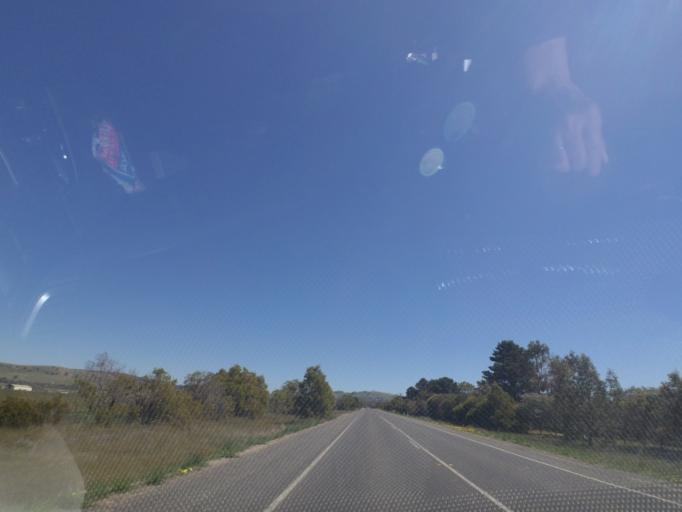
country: AU
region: Victoria
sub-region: Hume
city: Sunbury
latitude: -37.3078
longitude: 144.8404
